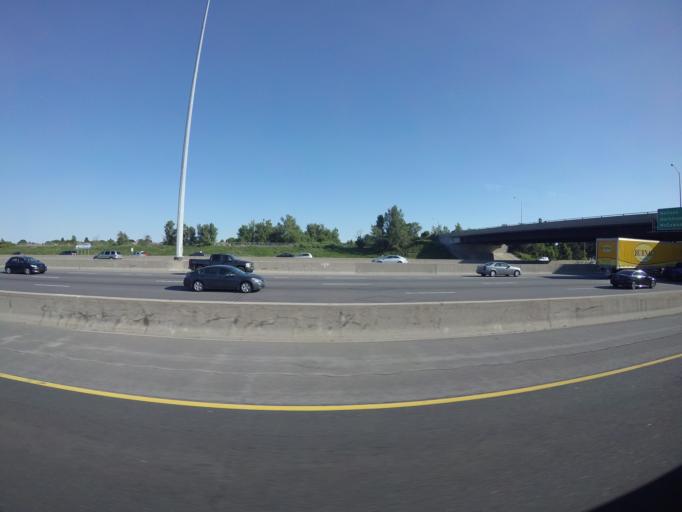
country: CA
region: Ontario
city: Scarborough
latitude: 43.7981
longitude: -79.1869
